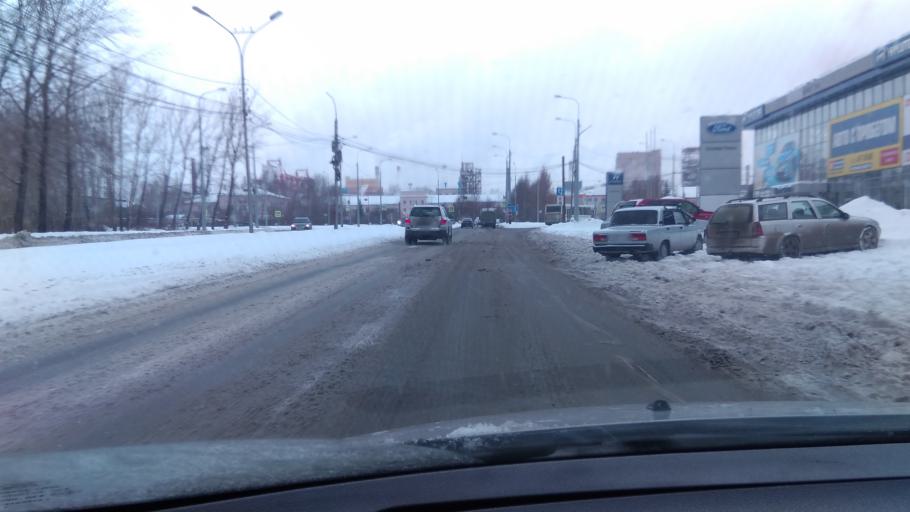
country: RU
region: Sverdlovsk
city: Nizhniy Tagil
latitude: 57.9076
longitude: 60.0092
